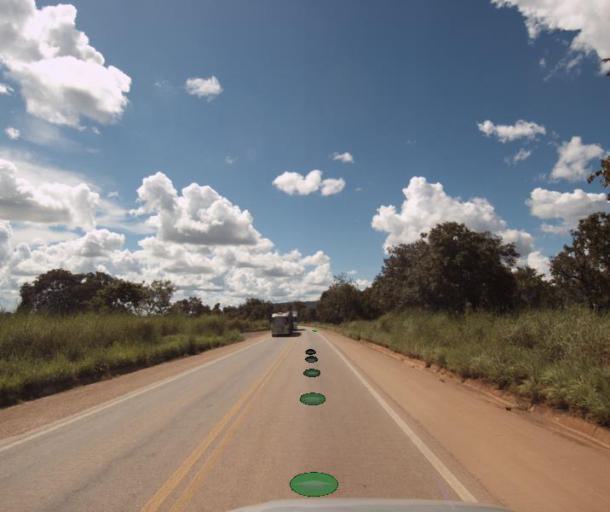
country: BR
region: Goias
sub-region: Porangatu
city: Porangatu
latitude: -13.6818
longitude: -49.0234
